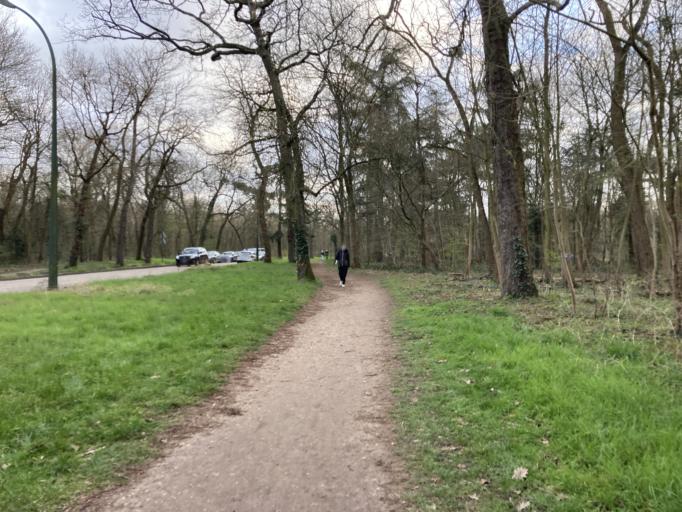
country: FR
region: Ile-de-France
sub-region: Departement des Hauts-de-Seine
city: Neuilly-sur-Seine
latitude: 48.8748
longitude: 2.2634
